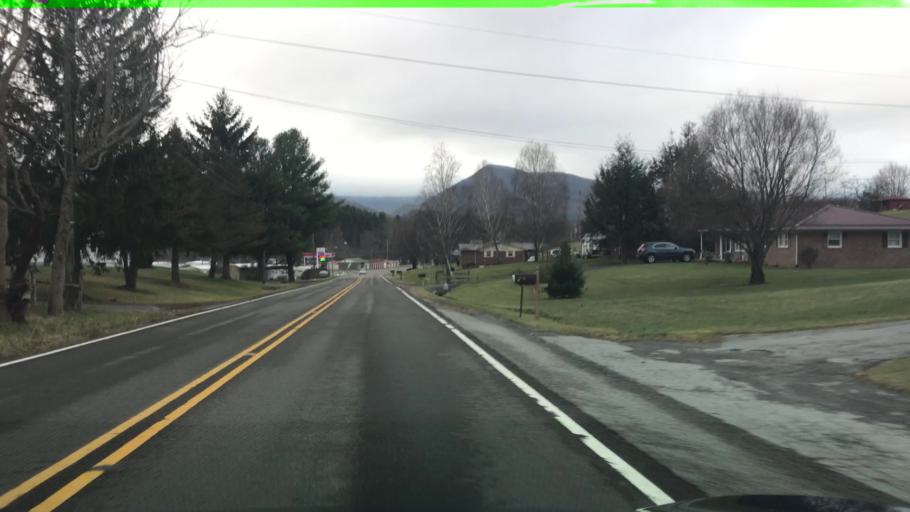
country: US
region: Virginia
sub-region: Smyth County
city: Atkins
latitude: 36.7813
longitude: -81.4068
